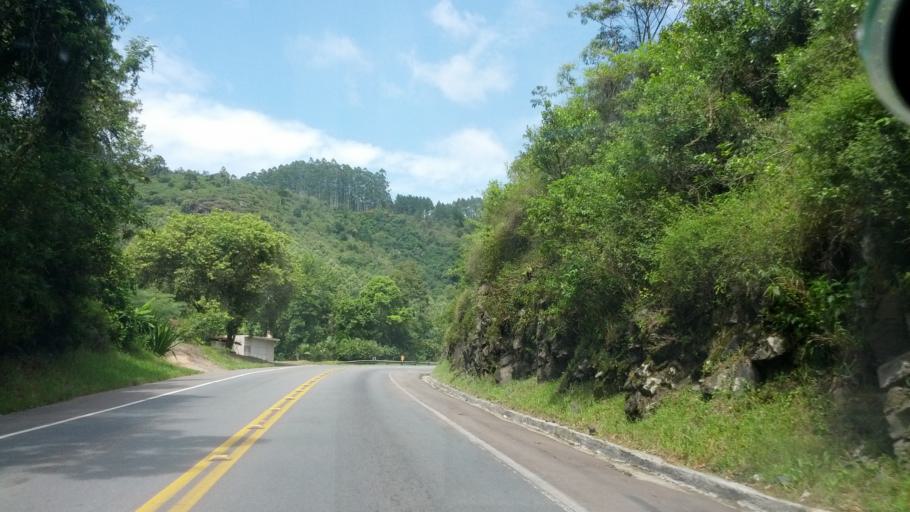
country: BR
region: Santa Catarina
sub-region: Ibirama
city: Ibirama
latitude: -27.0808
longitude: -49.5000
